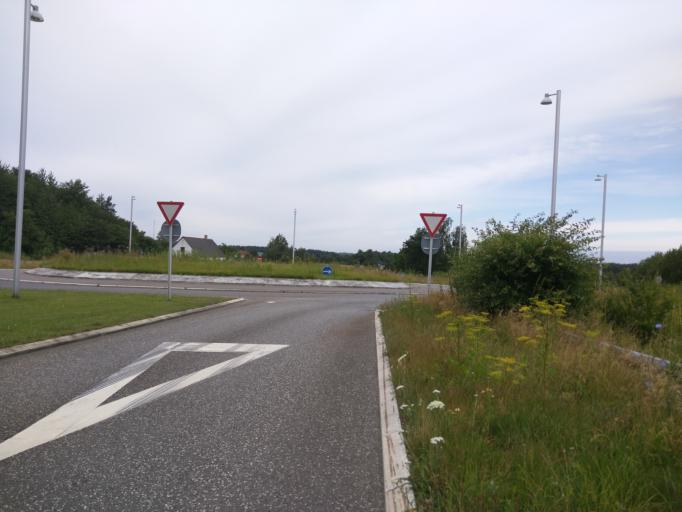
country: DK
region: Zealand
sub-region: Kalundborg Kommune
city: Svebolle
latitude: 55.6692
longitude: 11.3477
